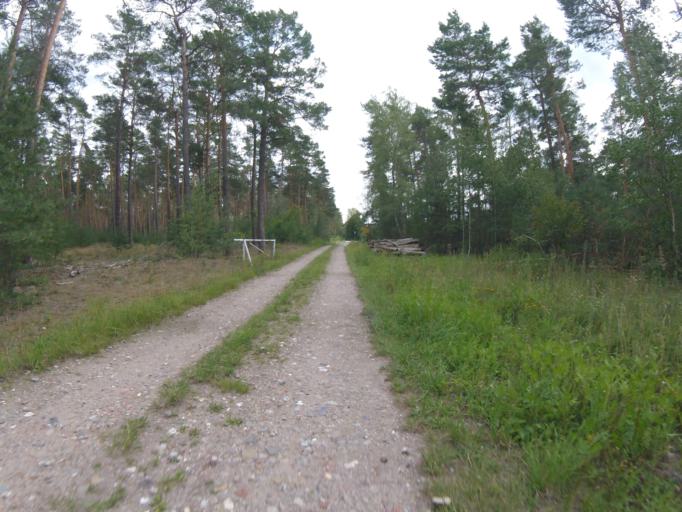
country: DE
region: Brandenburg
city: Halbe
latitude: 52.1179
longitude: 13.6994
